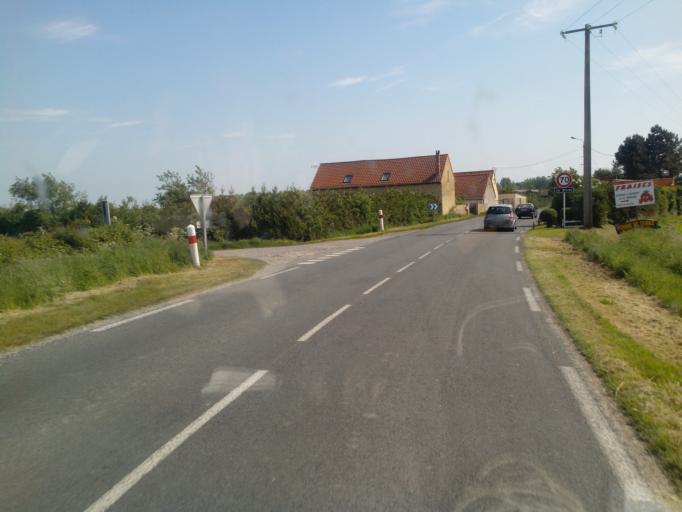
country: FR
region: Picardie
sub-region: Departement de la Somme
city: Quend
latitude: 50.3381
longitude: 1.6446
